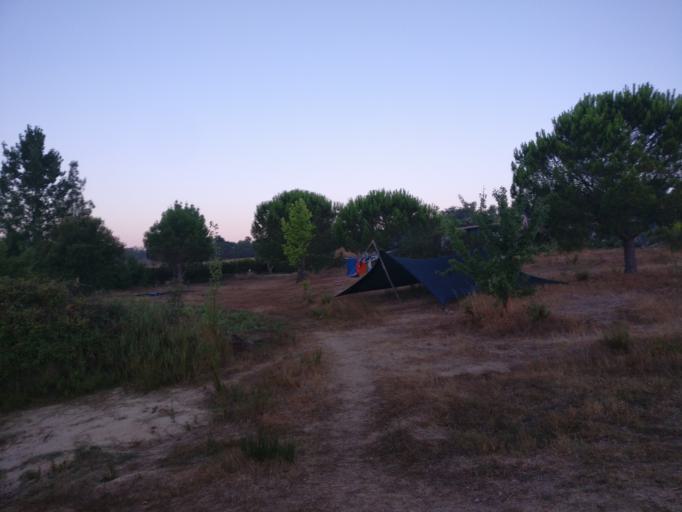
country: PT
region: Beja
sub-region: Odemira
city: Odemira
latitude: 37.7185
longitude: -8.5200
